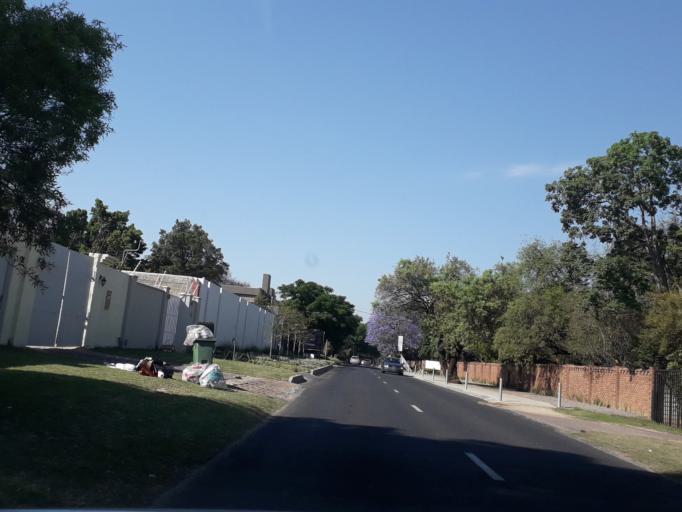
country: ZA
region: Gauteng
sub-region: City of Johannesburg Metropolitan Municipality
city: Midrand
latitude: -26.0419
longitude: 28.0342
